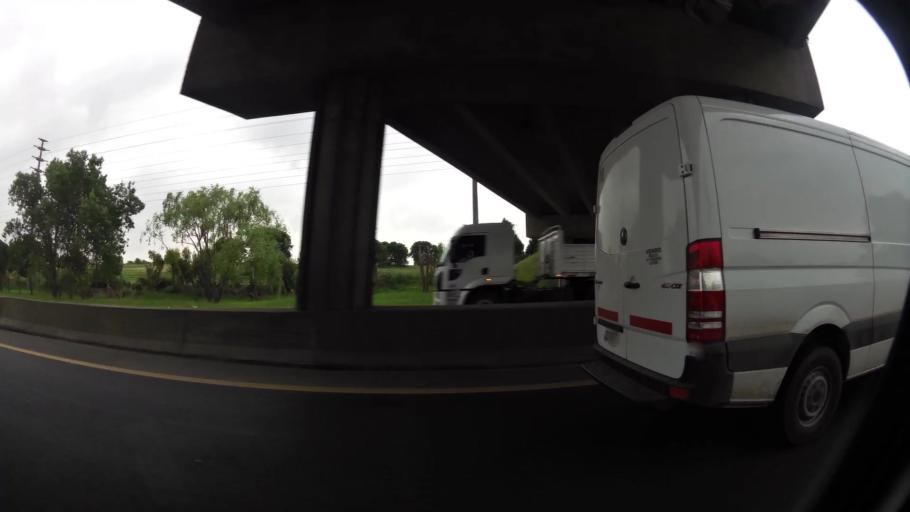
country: AR
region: Buenos Aires
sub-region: Partido de Quilmes
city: Quilmes
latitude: -34.6870
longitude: -58.2977
